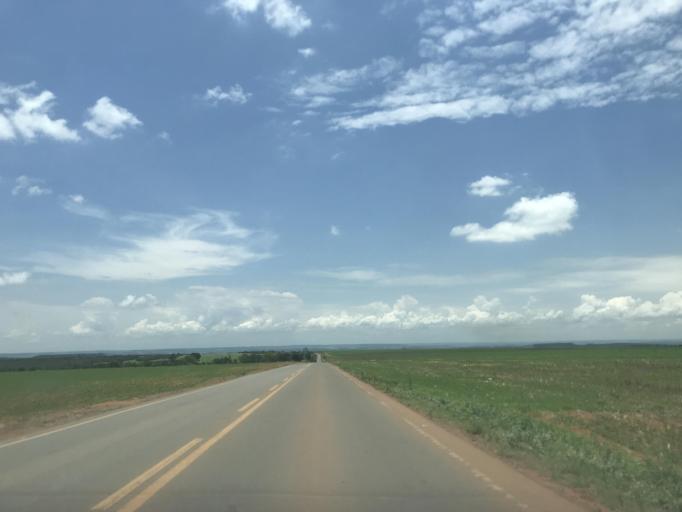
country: BR
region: Goias
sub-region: Vianopolis
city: Vianopolis
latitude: -16.5556
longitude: -48.2771
